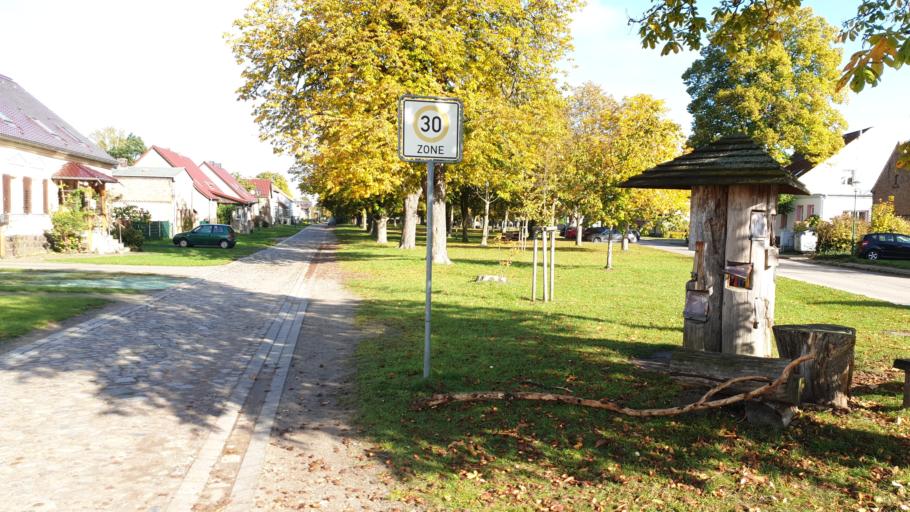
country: DE
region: Brandenburg
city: Liepe
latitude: 52.9099
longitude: 13.9601
